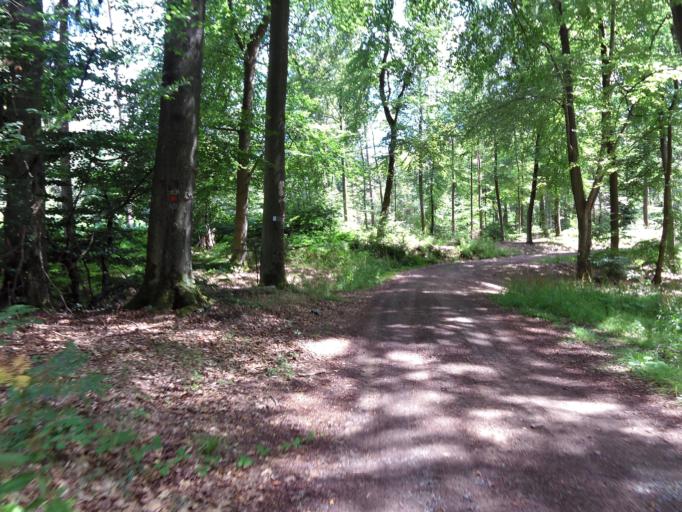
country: DE
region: Rheinland-Pfalz
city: Altleiningen
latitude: 49.4703
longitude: 8.0643
